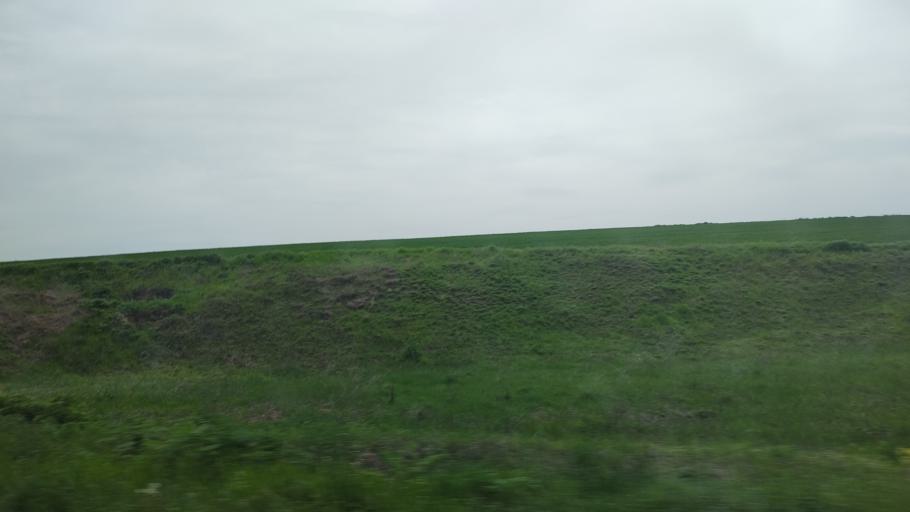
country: RO
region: Constanta
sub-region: Comuna Deleni
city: Pietreni
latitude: 44.0834
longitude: 28.1212
